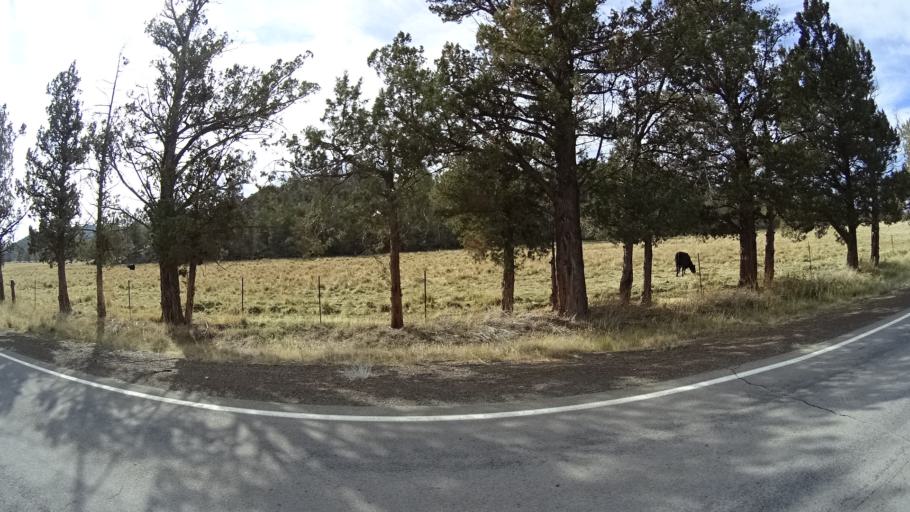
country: US
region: California
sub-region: Siskiyou County
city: Weed
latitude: 41.5774
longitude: -122.3962
